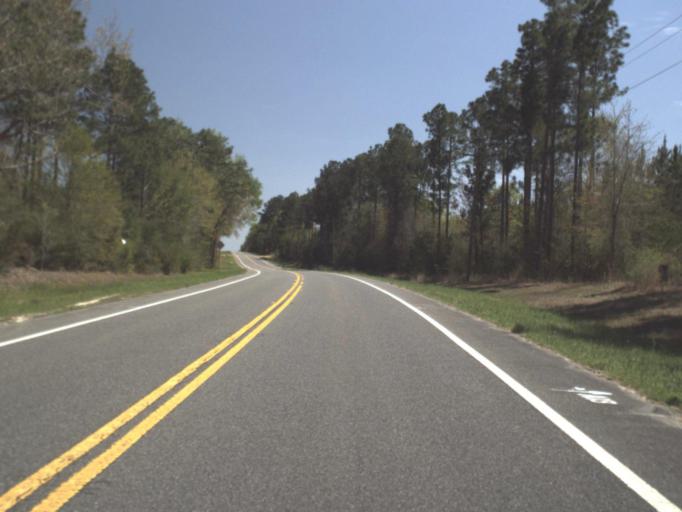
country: US
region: Alabama
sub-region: Geneva County
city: Geneva
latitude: 30.9625
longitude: -85.9958
